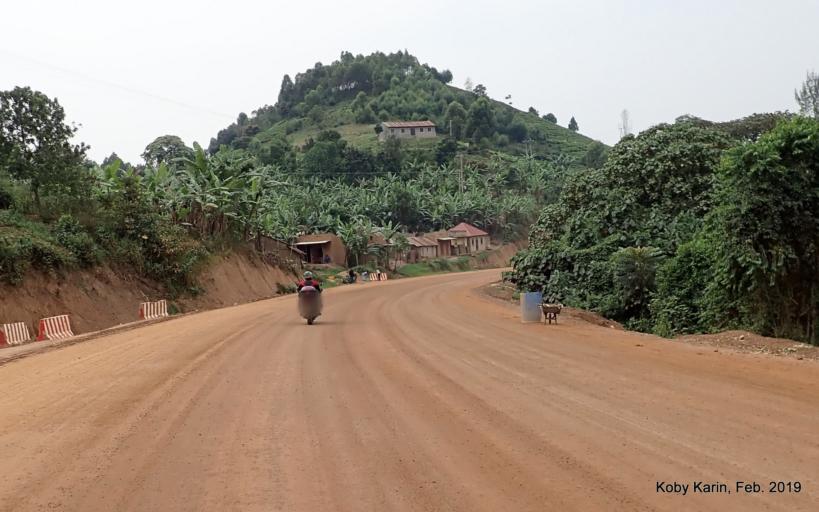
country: UG
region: Western Region
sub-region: Rubirizi District
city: Rubirizi
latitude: -0.3732
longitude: 30.1155
